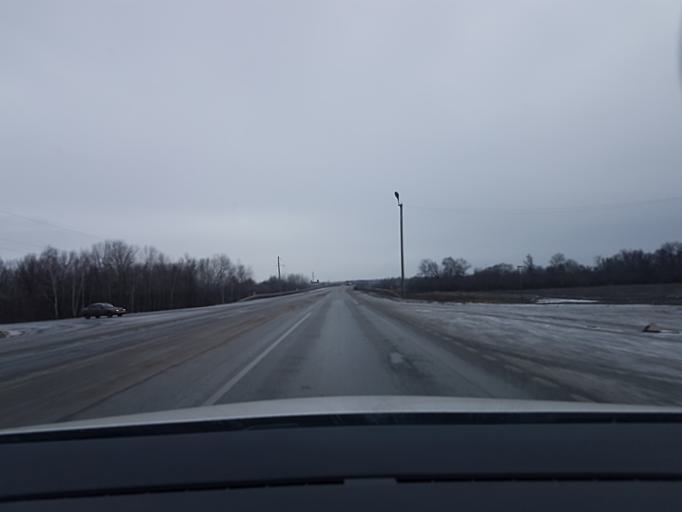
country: RU
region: Tambov
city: Zavoronezhskoye
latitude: 52.9538
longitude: 40.5801
